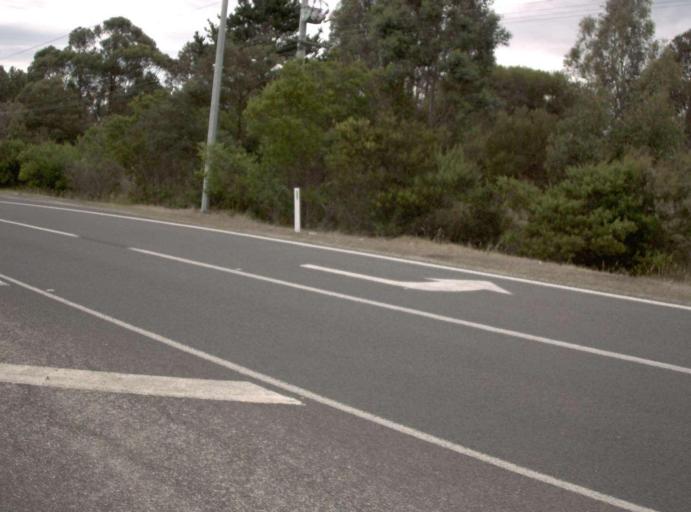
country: AU
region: Victoria
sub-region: Wellington
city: Sale
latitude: -38.1614
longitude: 147.0859
